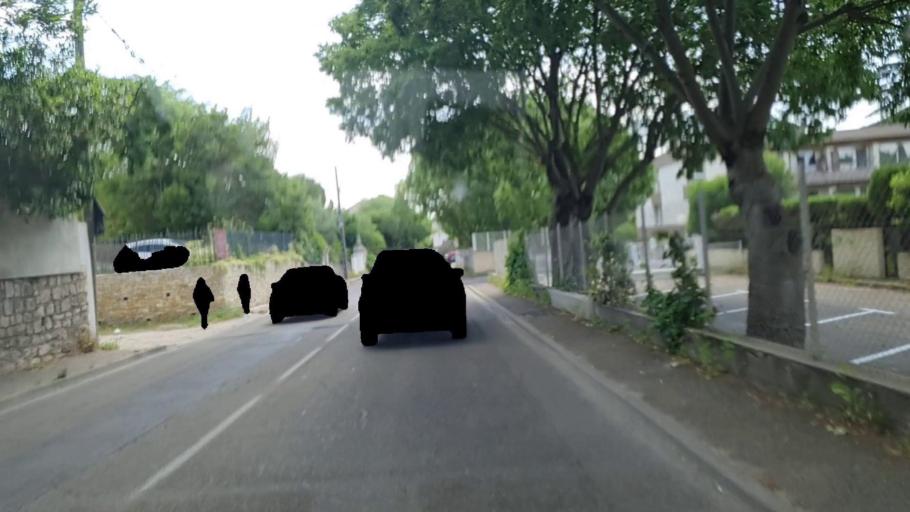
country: FR
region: Languedoc-Roussillon
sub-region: Departement du Gard
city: Nimes
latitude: 43.8367
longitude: 4.3350
